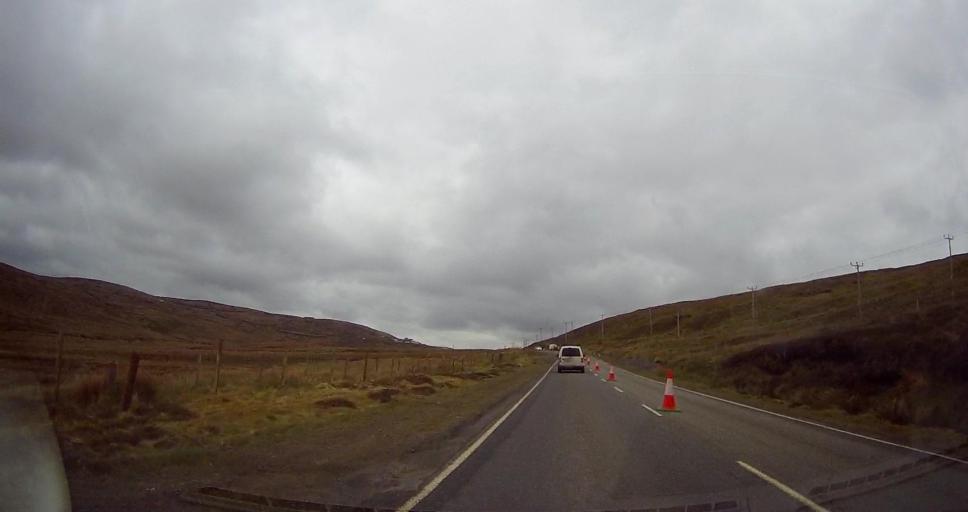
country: GB
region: Scotland
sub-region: Shetland Islands
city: Lerwick
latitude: 60.3353
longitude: -1.2534
